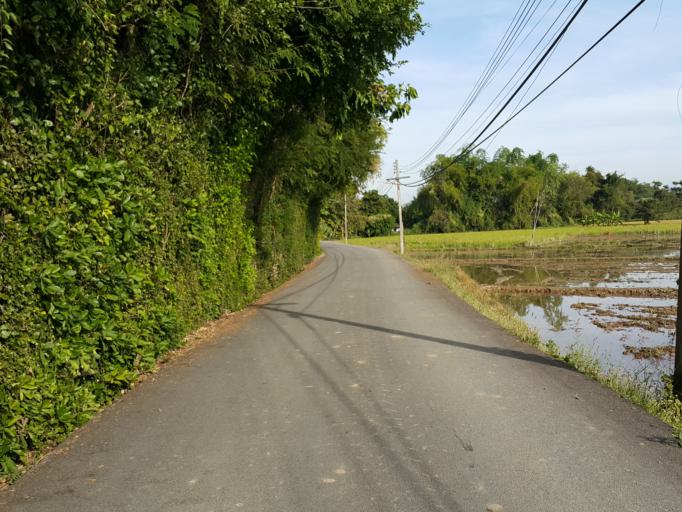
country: TH
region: Chiang Mai
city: San Kamphaeng
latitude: 18.7866
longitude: 99.1061
